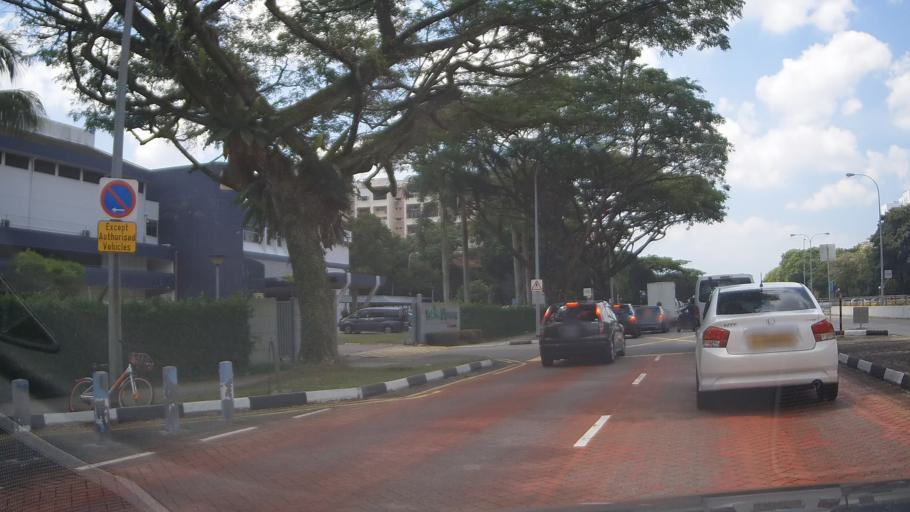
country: MY
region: Johor
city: Johor Bahru
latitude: 1.3511
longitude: 103.7283
